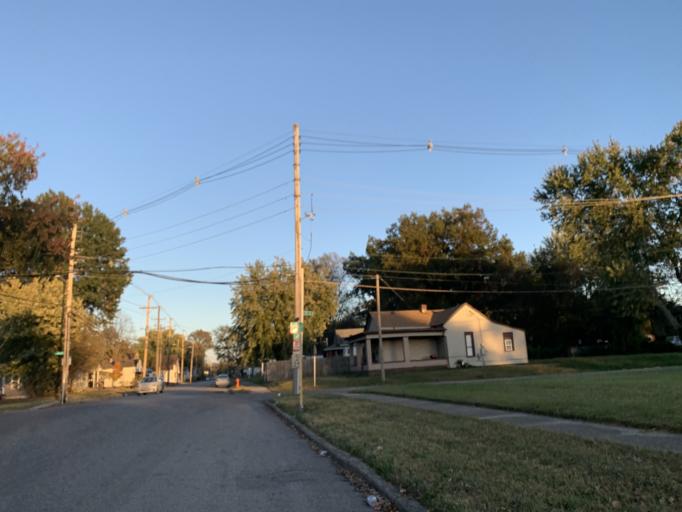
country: US
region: Kentucky
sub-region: Jefferson County
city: Shively
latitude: 38.2321
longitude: -85.8087
